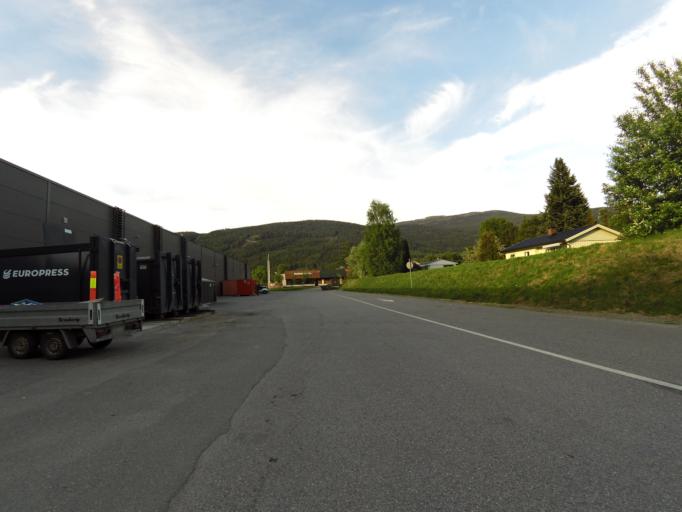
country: NO
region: Buskerud
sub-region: Fla
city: Fla
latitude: 60.4302
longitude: 9.4583
